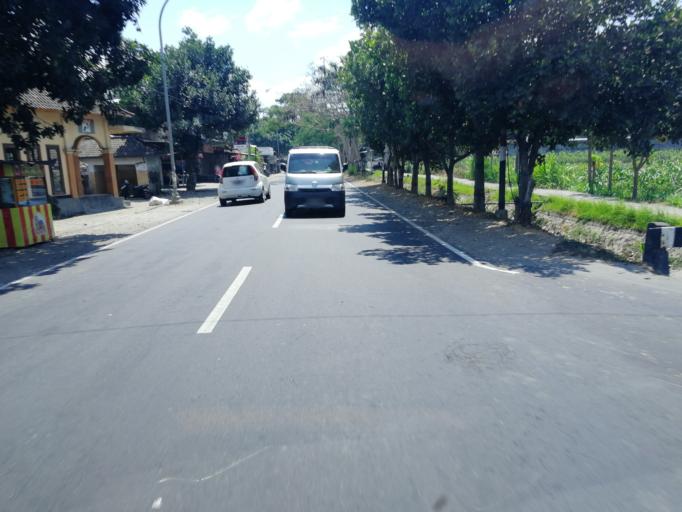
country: ID
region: West Nusa Tenggara
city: Jelateng Timur
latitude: -8.7001
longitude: 116.1024
